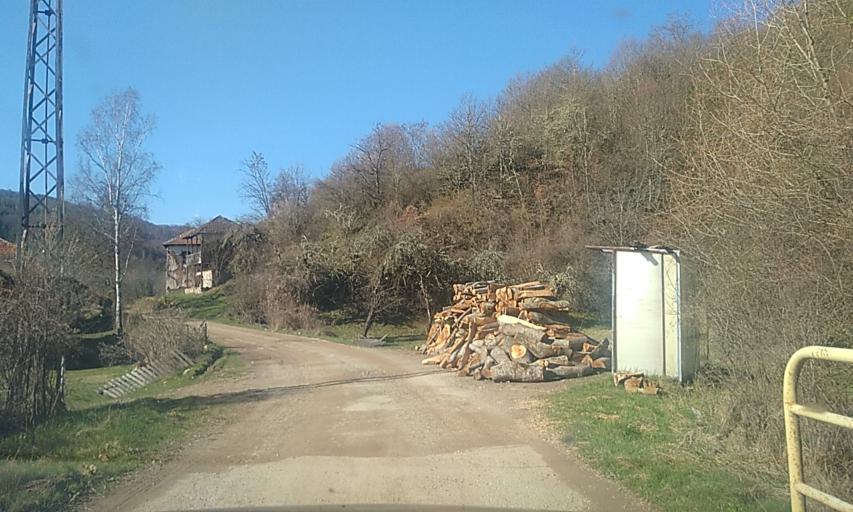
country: RS
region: Central Serbia
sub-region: Pcinjski Okrug
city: Bosilegrad
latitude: 42.3575
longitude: 22.4066
